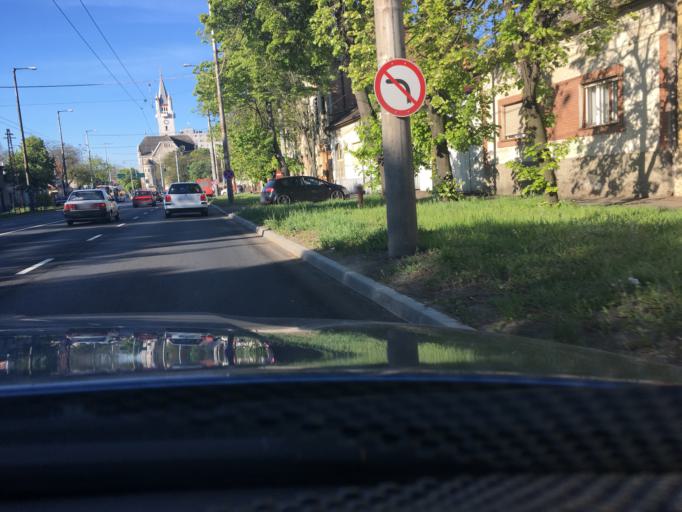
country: HU
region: Hajdu-Bihar
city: Debrecen
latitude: 47.5399
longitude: 21.6396
